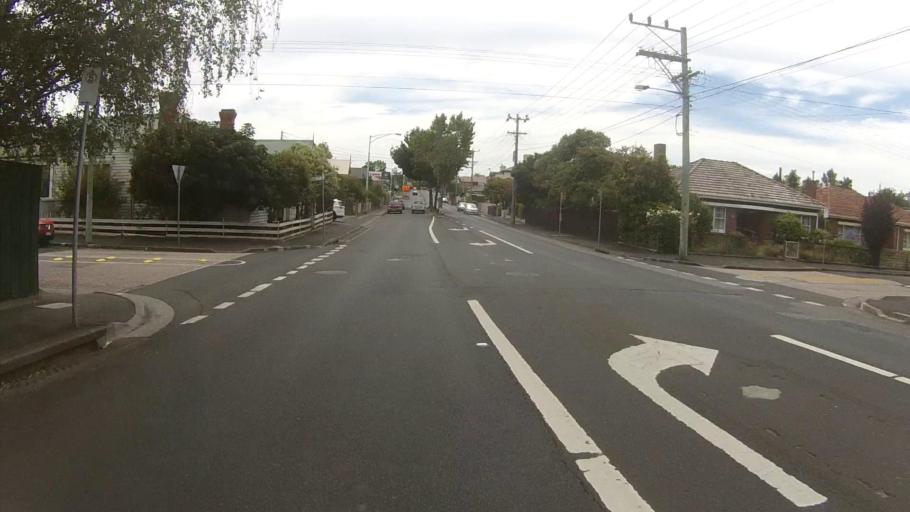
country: AU
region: Tasmania
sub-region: Hobart
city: Sandy Bay
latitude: -42.8985
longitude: 147.3241
